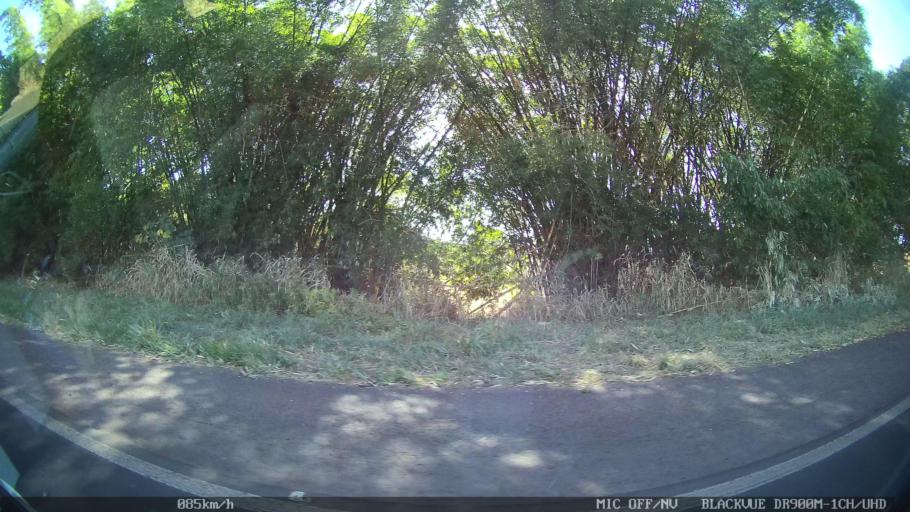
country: BR
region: Sao Paulo
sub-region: Barretos
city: Barretos
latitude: -20.6068
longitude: -48.7428
